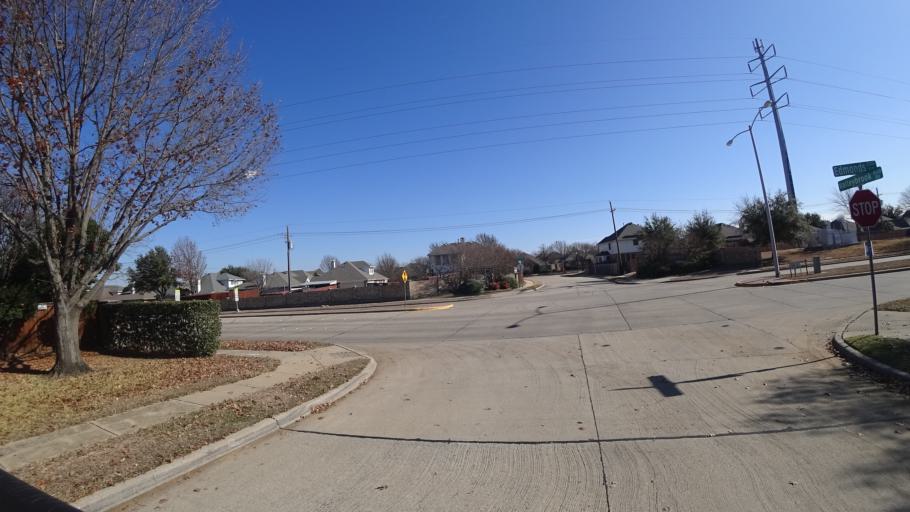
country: US
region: Texas
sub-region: Denton County
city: Lewisville
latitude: 33.0084
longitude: -97.0053
